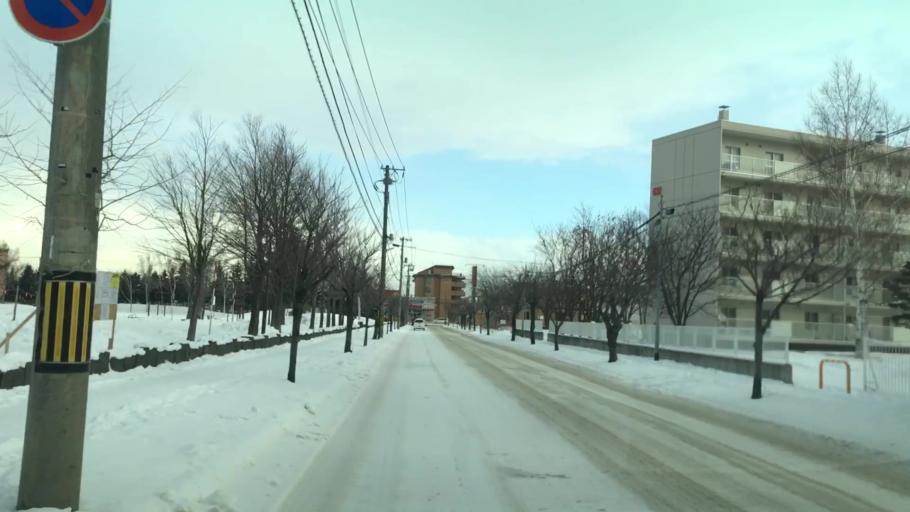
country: JP
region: Hokkaido
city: Sapporo
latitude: 43.0905
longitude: 141.3052
